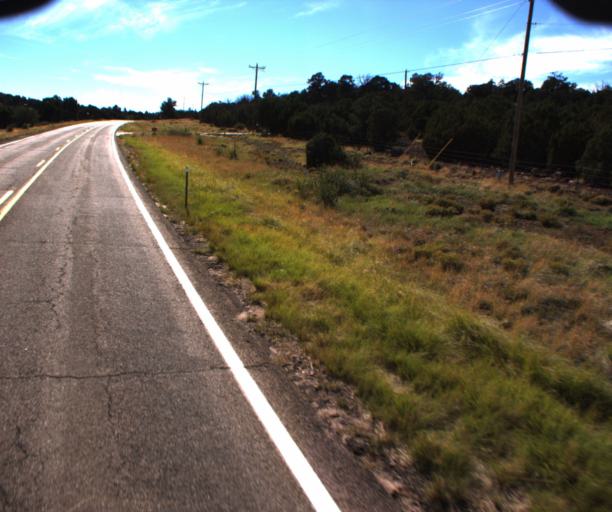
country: US
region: Arizona
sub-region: Navajo County
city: White Mountain Lake
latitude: 34.3135
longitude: -109.7685
